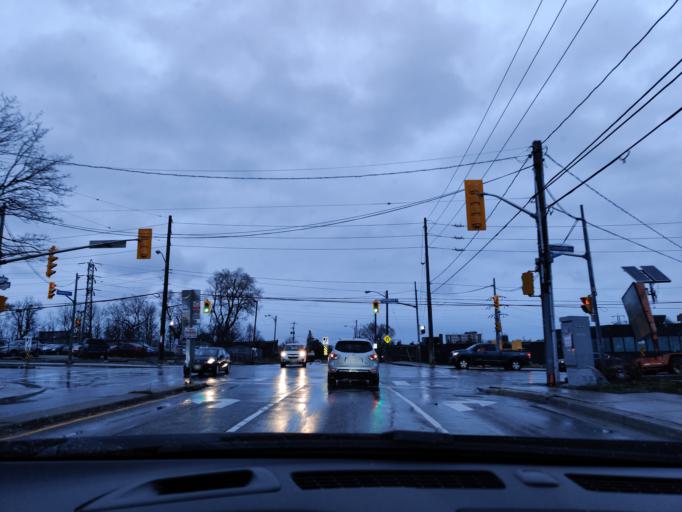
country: CA
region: Ontario
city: Toronto
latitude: 43.6987
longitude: -79.4636
